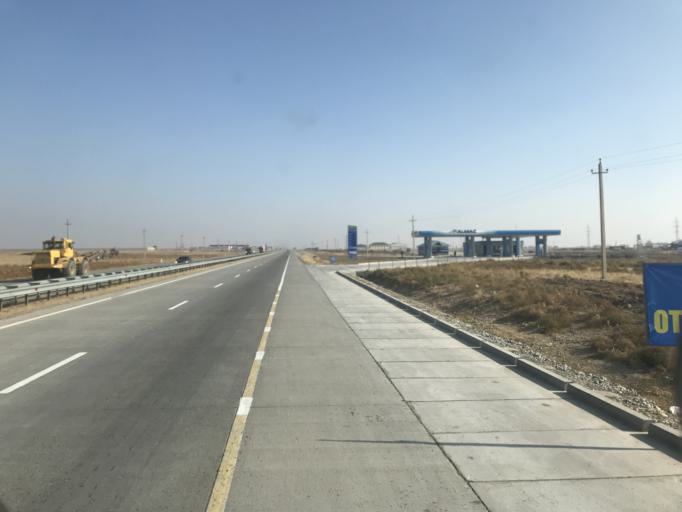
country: KZ
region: Ongtustik Qazaqstan
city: Shymkent
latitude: 42.4559
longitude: 69.6071
